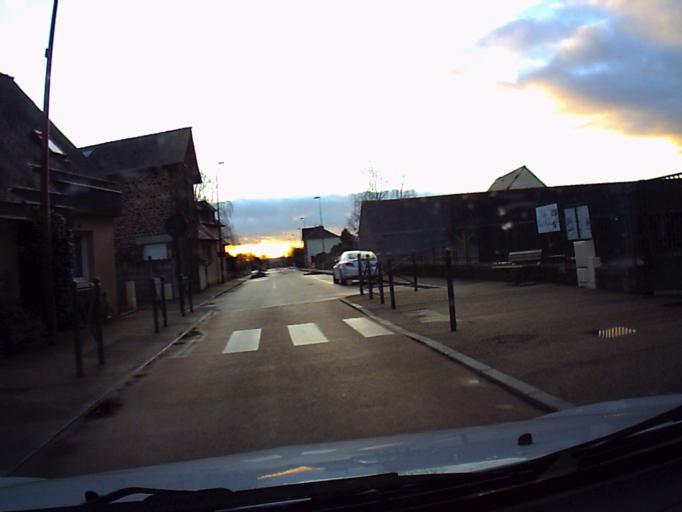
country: FR
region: Brittany
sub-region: Departement d'Ille-et-Vilaine
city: Bedee
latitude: 48.1795
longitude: -1.9473
